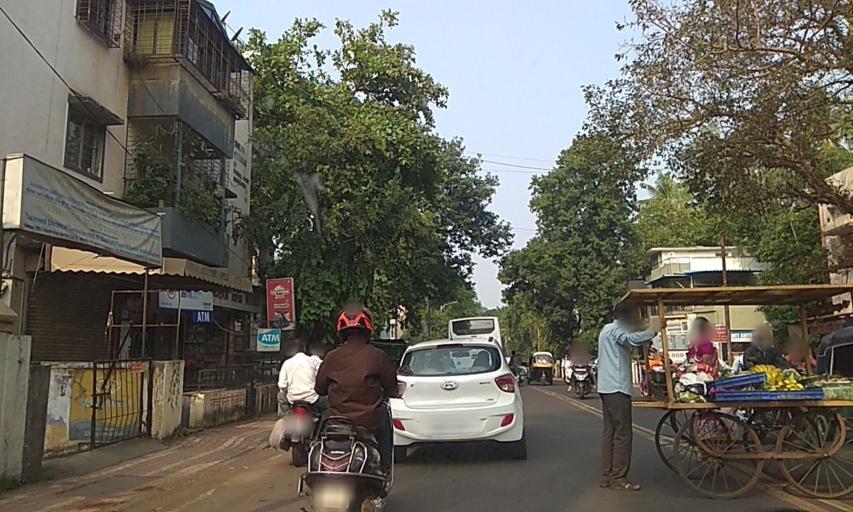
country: IN
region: Maharashtra
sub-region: Pune Division
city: Pune
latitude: 18.5049
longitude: 73.8414
